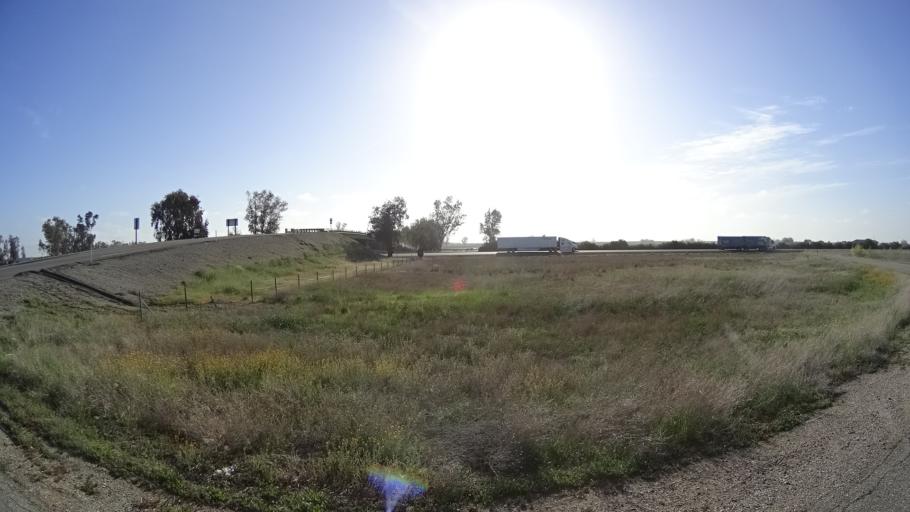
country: US
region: California
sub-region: Glenn County
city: Willows
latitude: 39.5820
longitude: -122.2121
